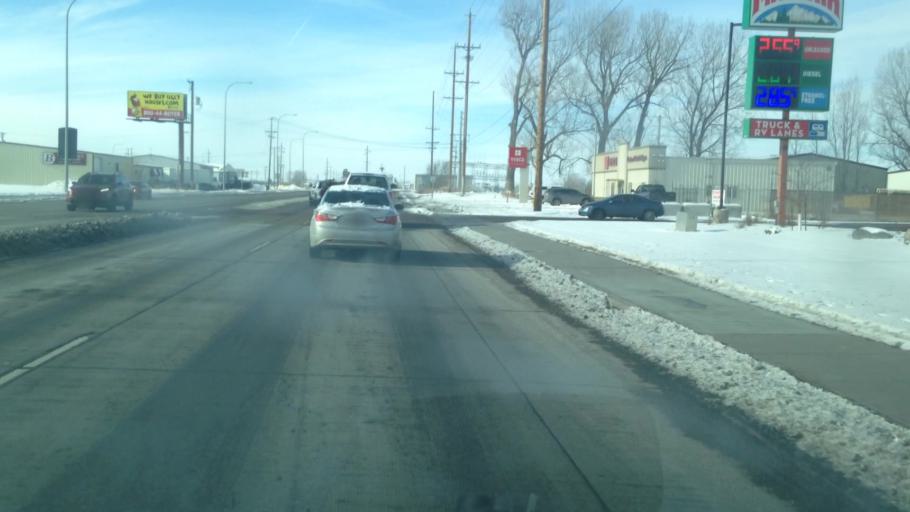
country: US
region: Idaho
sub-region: Bonneville County
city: Idaho Falls
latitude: 43.4684
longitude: -112.0568
